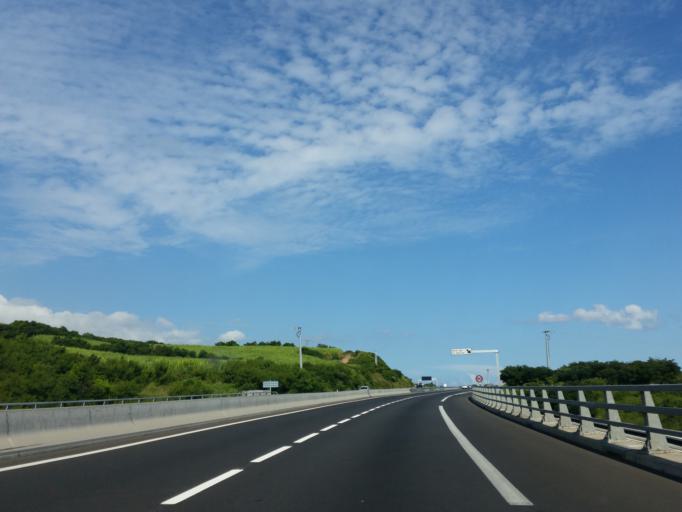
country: RE
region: Reunion
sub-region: Reunion
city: Trois-Bassins
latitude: -21.0834
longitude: 55.2559
